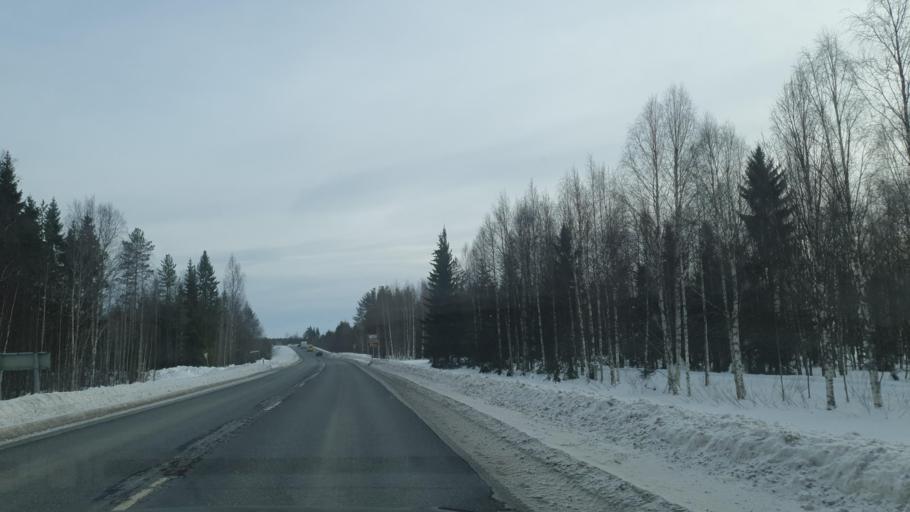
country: FI
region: Kainuu
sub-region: Kajaani
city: Kajaani
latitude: 64.4634
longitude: 27.4833
